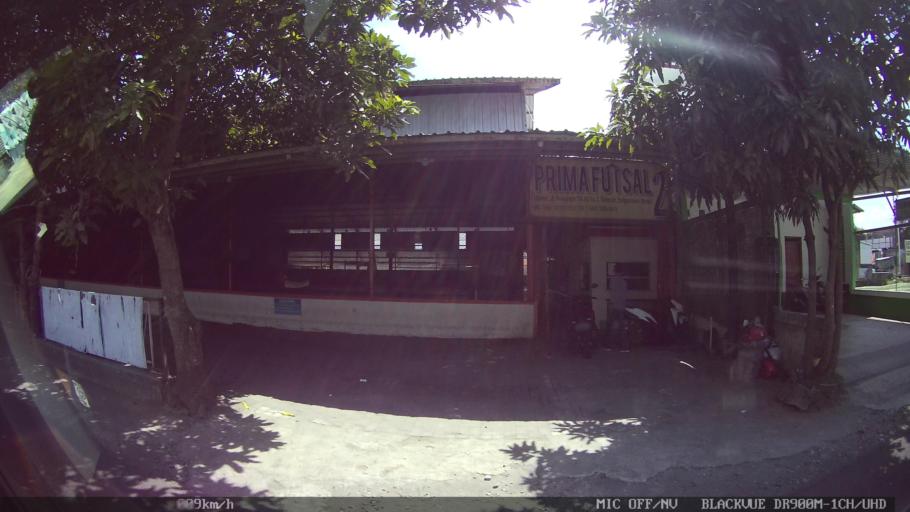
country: ID
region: Daerah Istimewa Yogyakarta
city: Sewon
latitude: -7.8434
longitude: 110.3909
